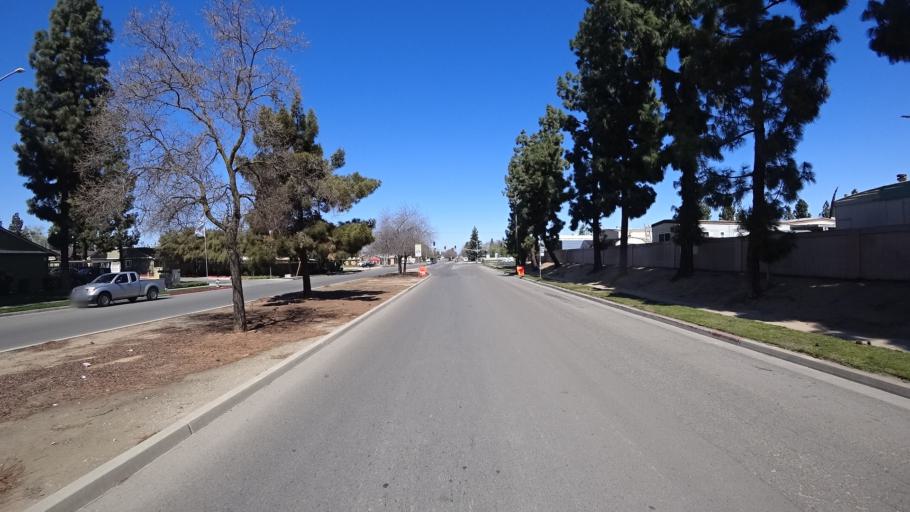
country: US
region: California
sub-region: Fresno County
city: West Park
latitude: 36.7634
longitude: -119.8443
